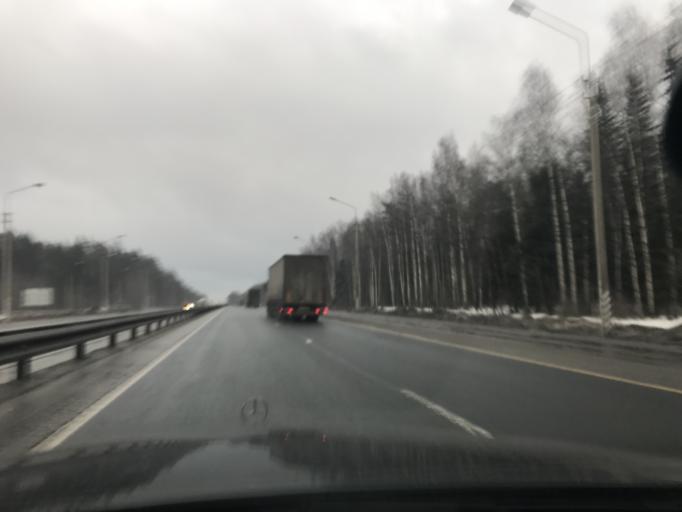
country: RU
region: Vladimir
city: Kameshkovo
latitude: 56.1947
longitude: 40.9623
